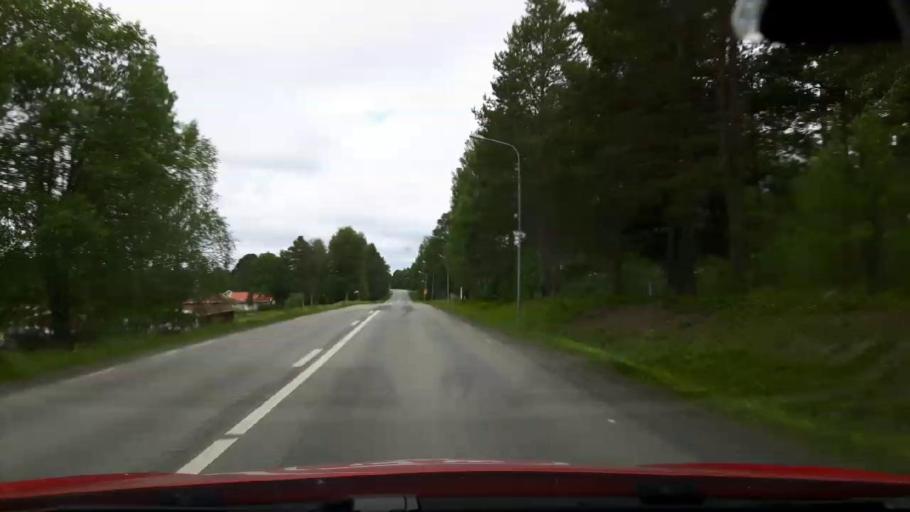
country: SE
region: Jaemtland
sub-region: Krokoms Kommun
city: Krokom
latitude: 63.2962
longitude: 14.4852
